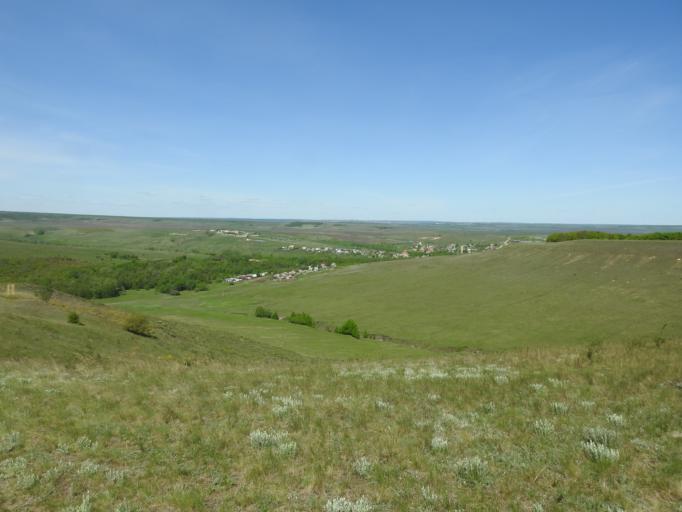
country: RU
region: Saratov
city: Krasnyy Oktyabr'
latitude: 51.5972
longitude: 45.7171
